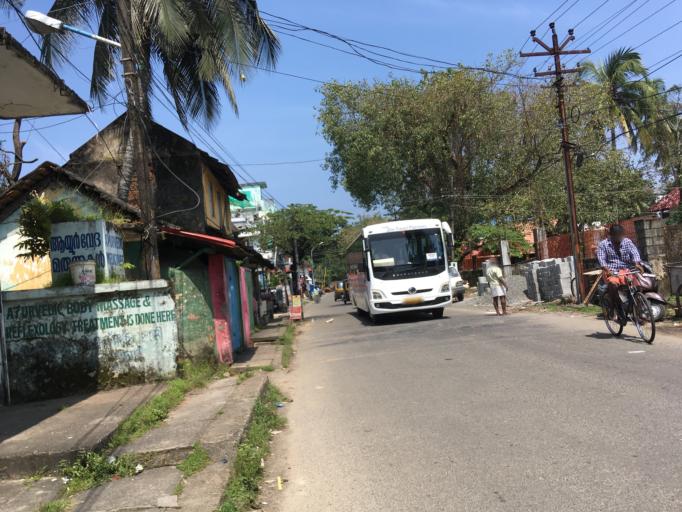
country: IN
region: Kerala
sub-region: Ernakulam
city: Cochin
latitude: 9.9571
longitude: 76.2448
